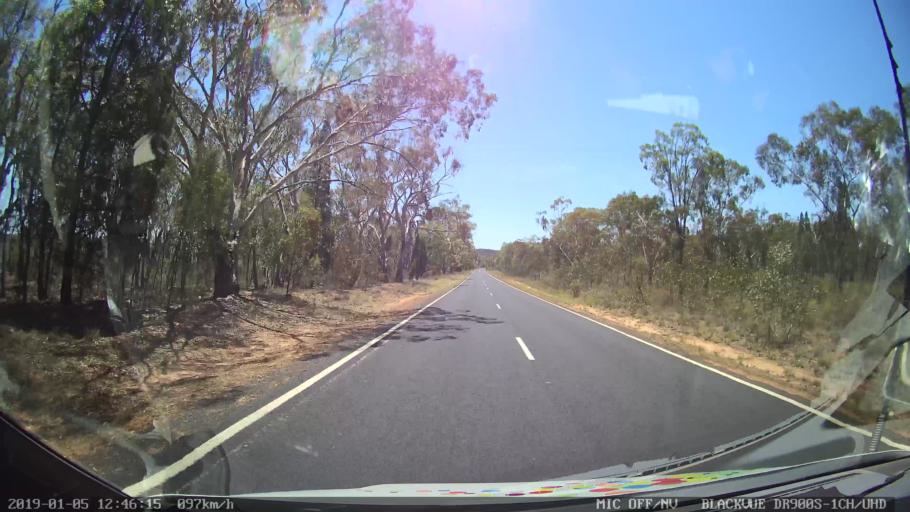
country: AU
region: New South Wales
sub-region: Warrumbungle Shire
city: Coonabarabran
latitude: -31.1198
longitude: 149.5602
